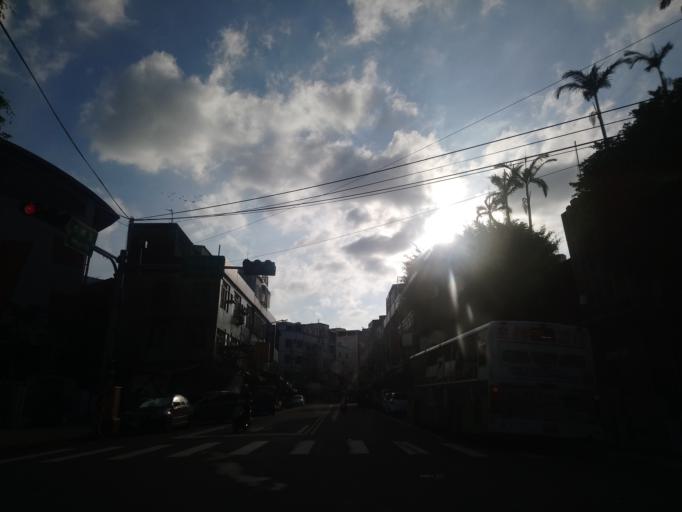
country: TW
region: Taiwan
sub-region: Hsinchu
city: Hsinchu
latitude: 24.7973
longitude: 120.9423
